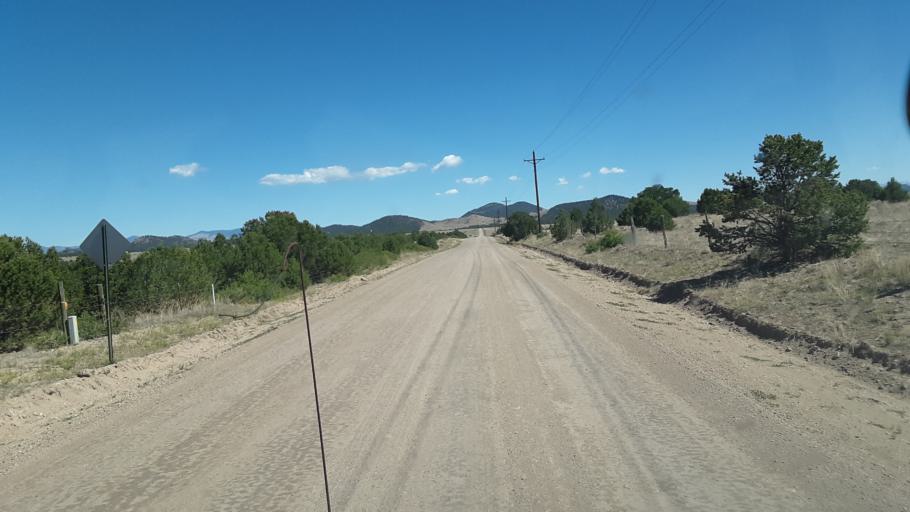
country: US
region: Colorado
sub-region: Custer County
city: Westcliffe
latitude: 38.2663
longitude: -105.5011
